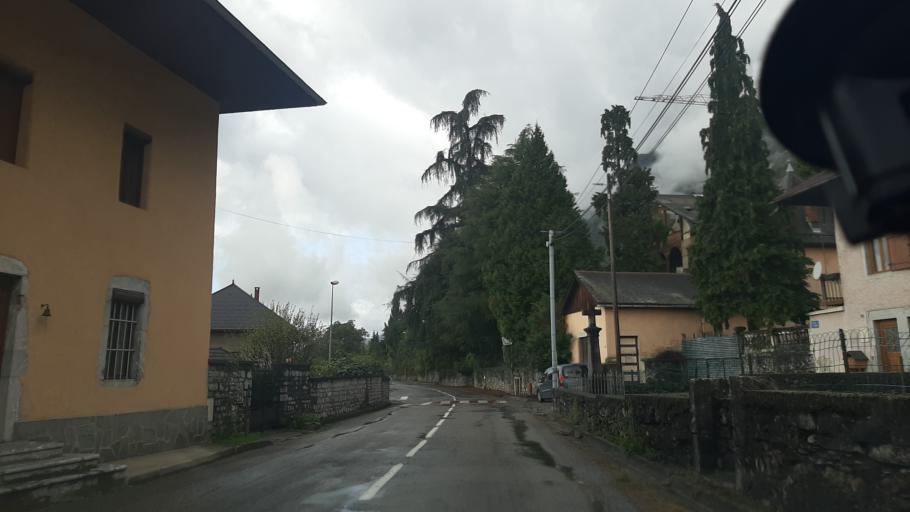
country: FR
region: Rhone-Alpes
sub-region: Departement de la Savoie
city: Gresy-sur-Isere
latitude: 45.6005
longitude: 6.2510
